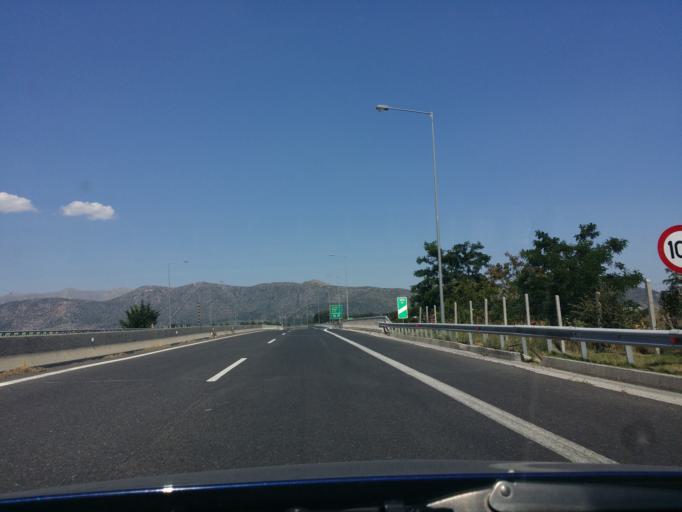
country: GR
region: Peloponnese
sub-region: Nomos Arkadias
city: Tripoli
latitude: 37.5004
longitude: 22.3947
